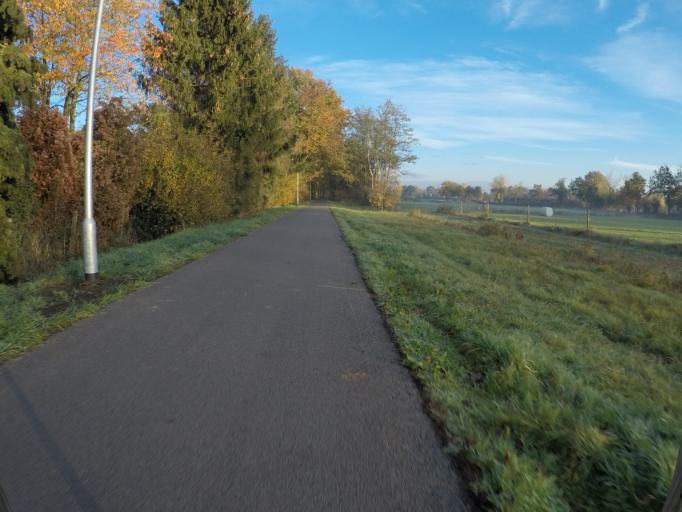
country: BE
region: Flanders
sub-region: Provincie Antwerpen
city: Olen
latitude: 51.1148
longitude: 4.8255
